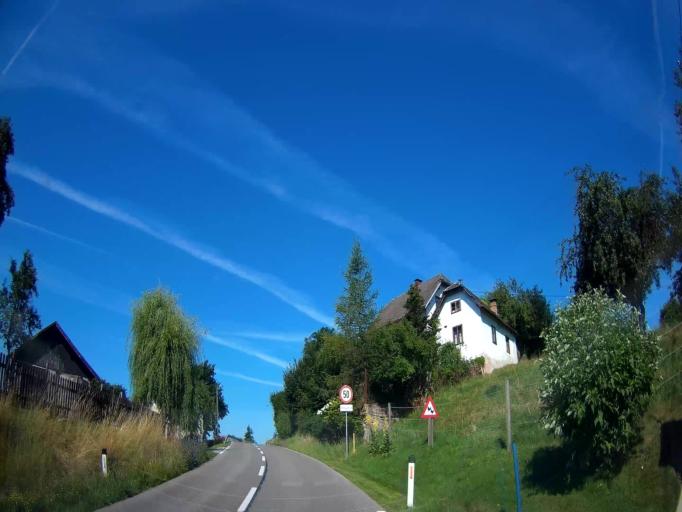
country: AT
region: Carinthia
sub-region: Politischer Bezirk Klagenfurt Land
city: Maria Saal
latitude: 46.6942
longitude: 14.3736
